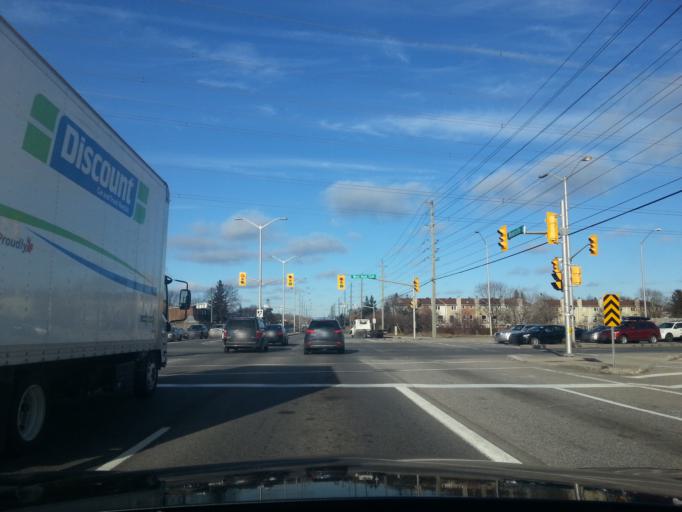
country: CA
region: Ontario
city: Bells Corners
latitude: 45.3285
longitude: -75.7487
